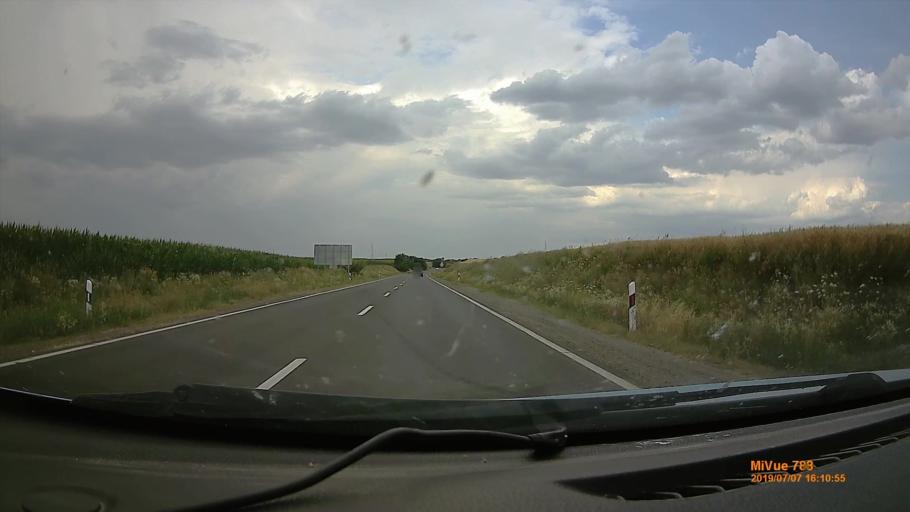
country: HU
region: Heves
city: Hatvan
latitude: 47.6704
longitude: 19.7184
